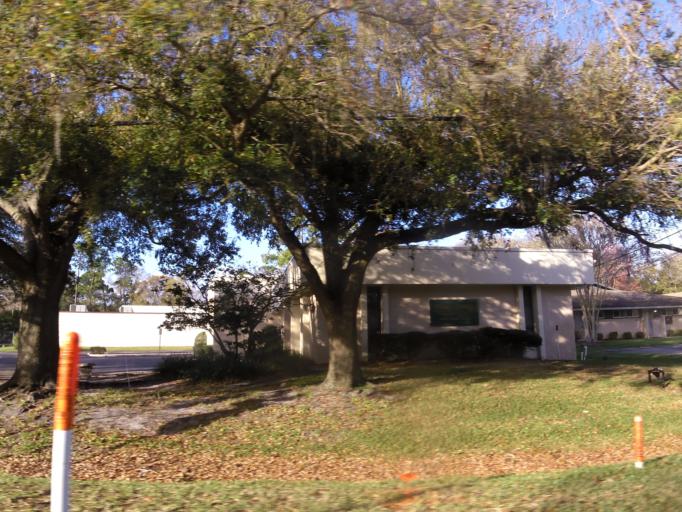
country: US
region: Florida
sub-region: Duval County
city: Jacksonville
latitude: 30.2518
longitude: -81.5941
